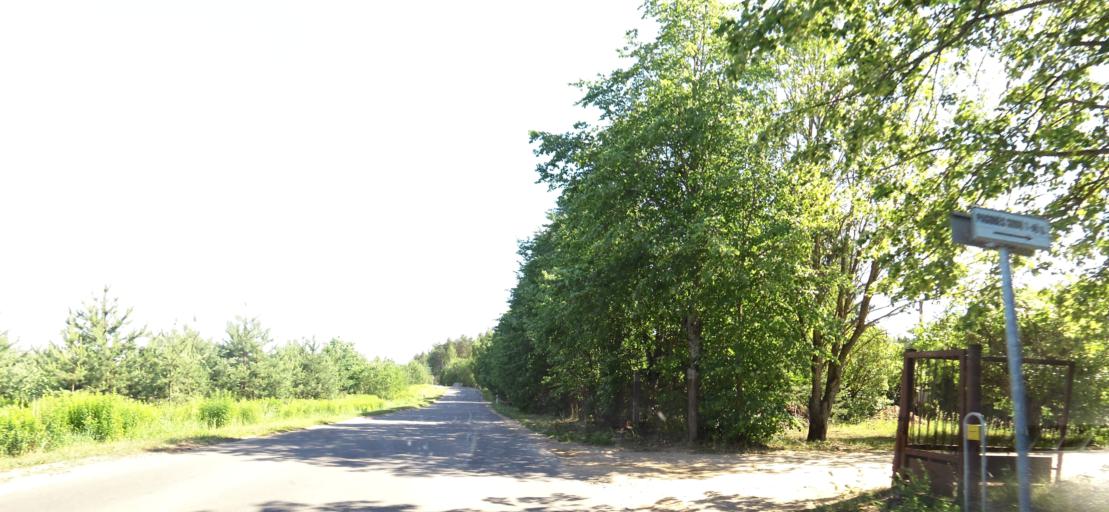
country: LT
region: Vilnius County
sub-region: Vilnius
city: Fabijoniskes
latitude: 54.8047
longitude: 25.3285
